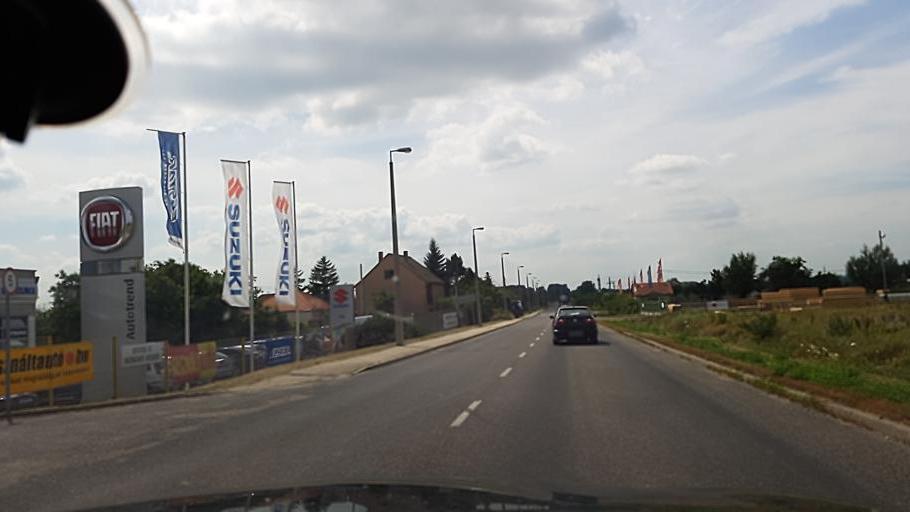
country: HU
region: Komarom-Esztergom
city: Dorog
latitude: 47.7495
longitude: 18.7270
